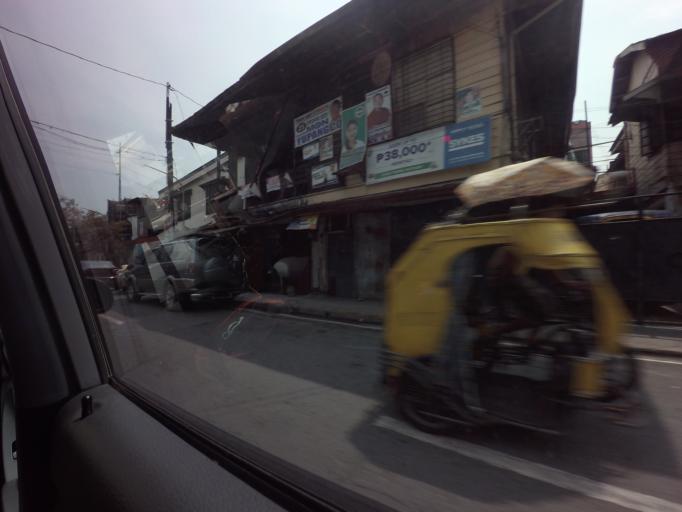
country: PH
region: Metro Manila
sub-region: City of Manila
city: Quiapo
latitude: 14.5736
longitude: 120.9952
